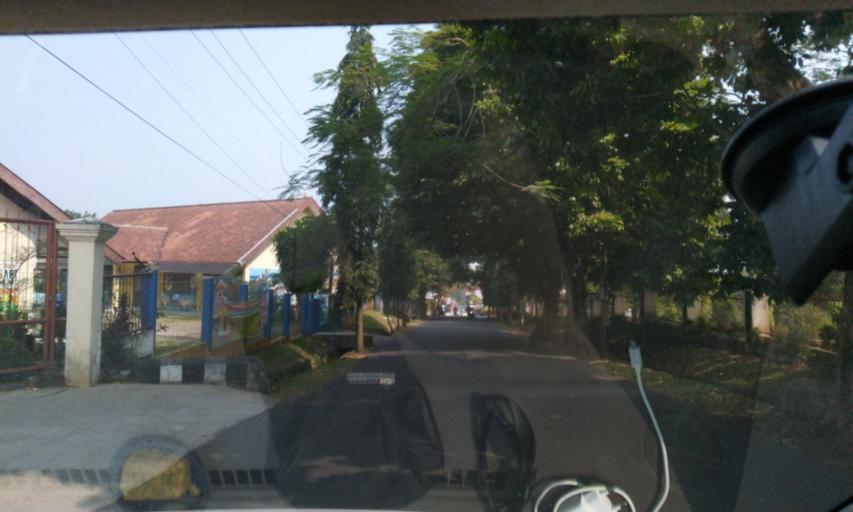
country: ID
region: West Java
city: Caringin
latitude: -6.6618
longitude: 106.8595
